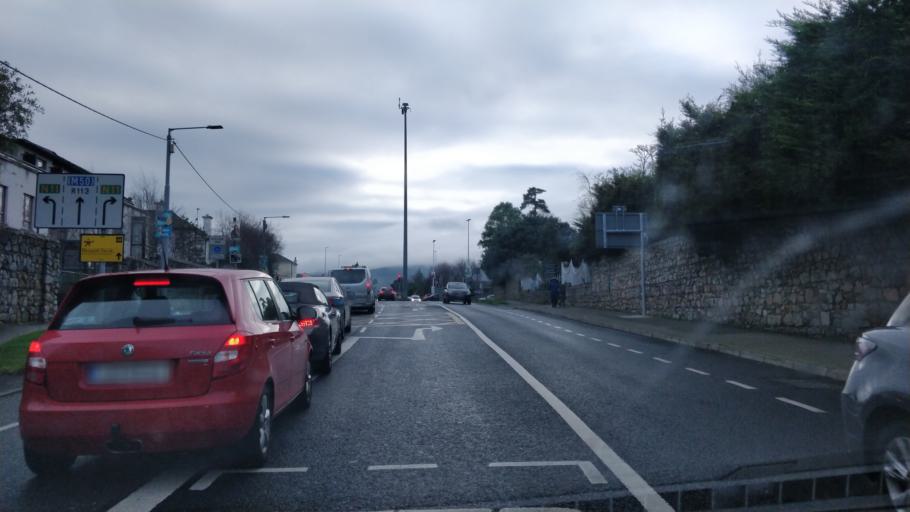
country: IE
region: Leinster
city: Foxrock
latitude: 53.2793
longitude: -6.1840
